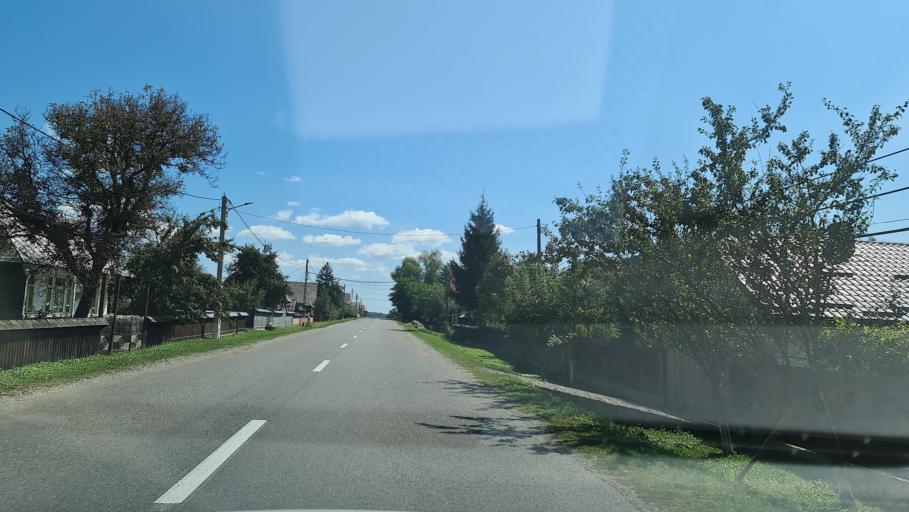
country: RO
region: Bacau
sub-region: Comuna Balcani
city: Frumoasa
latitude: 46.6573
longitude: 26.5492
